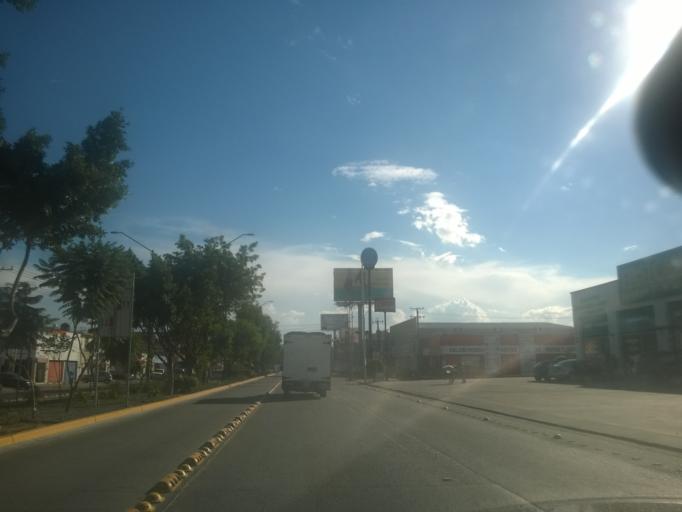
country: MX
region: Guanajuato
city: Leon
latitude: 21.1236
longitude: -101.6489
